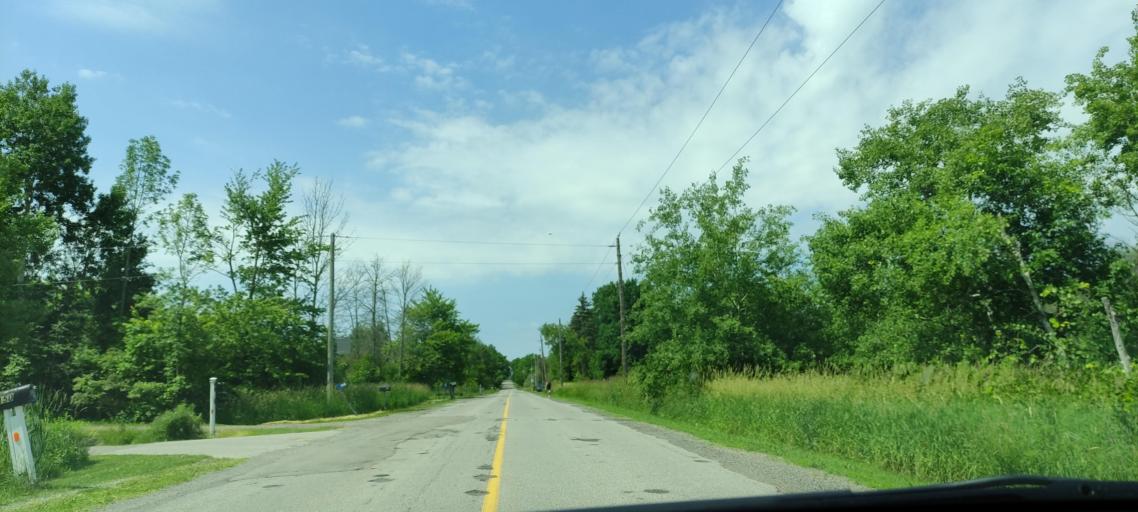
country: CA
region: Ontario
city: Burlington
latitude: 43.3633
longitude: -79.9614
